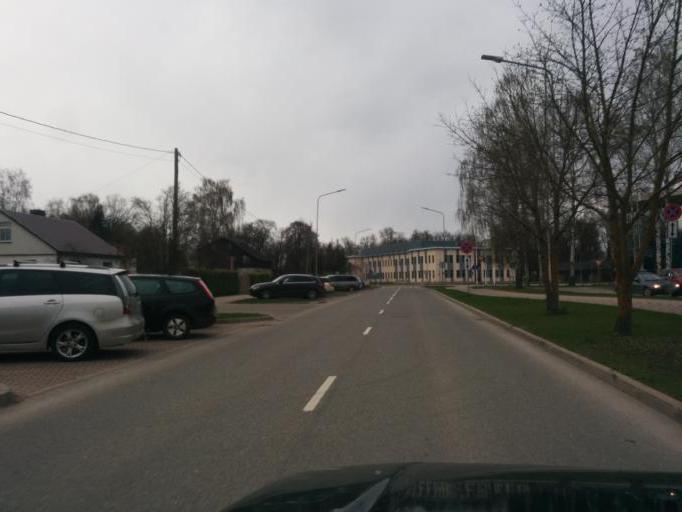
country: LV
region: Jelgava
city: Jelgava
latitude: 56.6601
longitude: 23.7537
